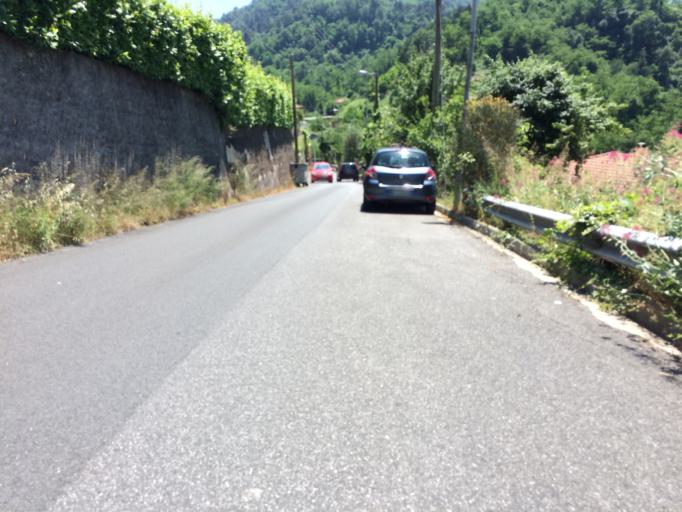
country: IT
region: Tuscany
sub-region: Provincia di Massa-Carrara
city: Massa
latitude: 44.0713
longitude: 10.1095
